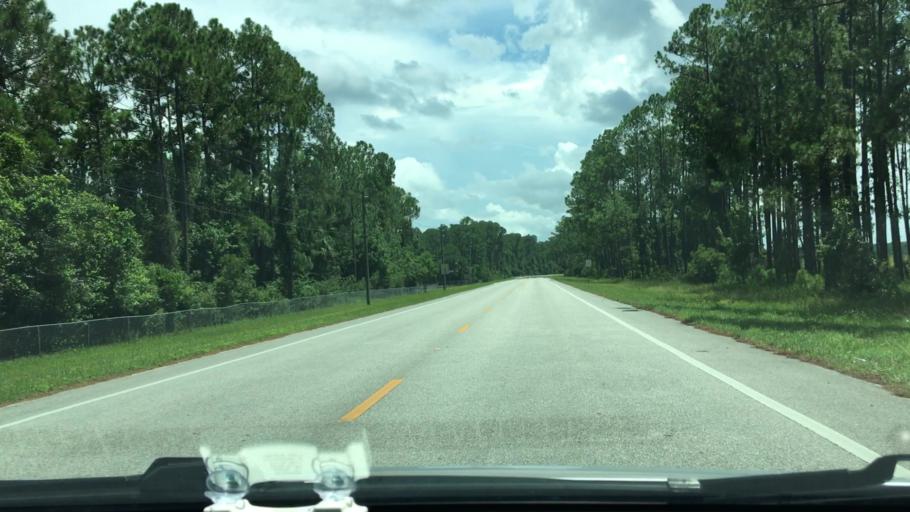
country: US
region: Florida
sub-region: Volusia County
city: Samsula-Spruce Creek
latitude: 29.0316
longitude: -81.0666
